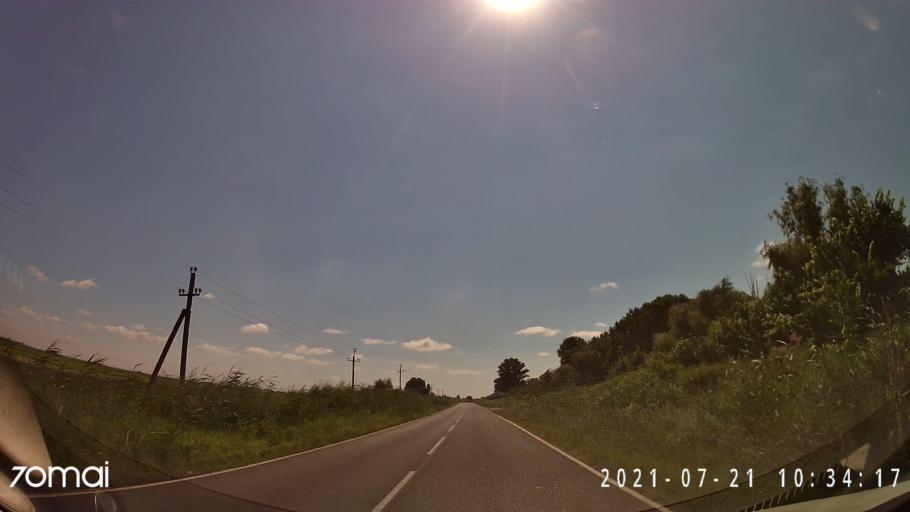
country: RO
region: Tulcea
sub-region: Oras Isaccea
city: Isaccea
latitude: 45.2960
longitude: 28.4438
